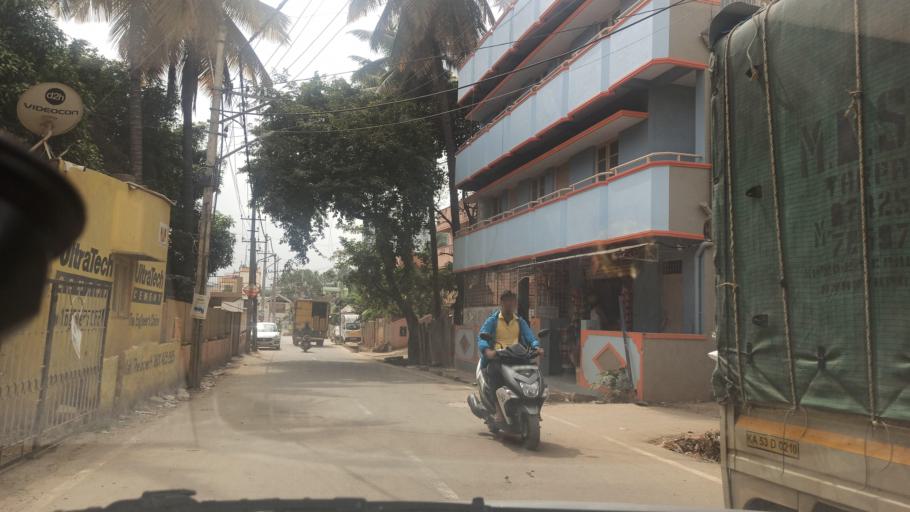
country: IN
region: Karnataka
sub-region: Bangalore Urban
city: Yelahanka
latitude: 13.0497
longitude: 77.6105
